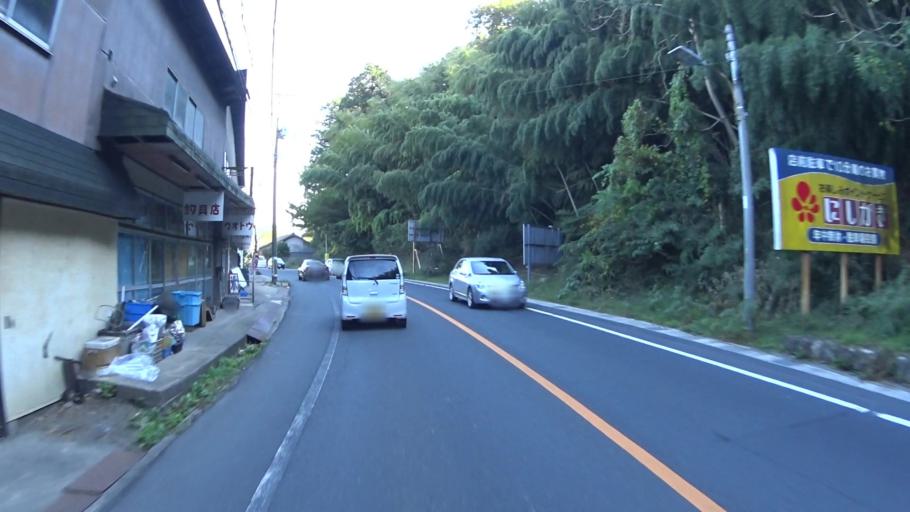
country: JP
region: Kyoto
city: Miyazu
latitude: 35.6645
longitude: 135.0287
